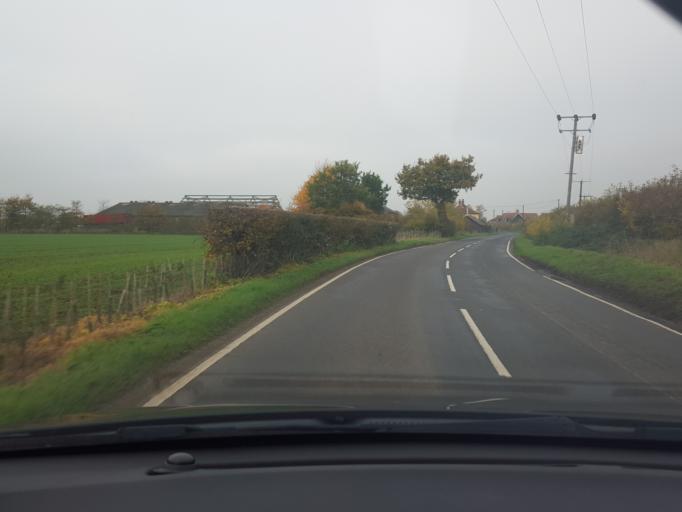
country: GB
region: England
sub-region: Essex
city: Alresford
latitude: 51.8999
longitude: 1.0137
